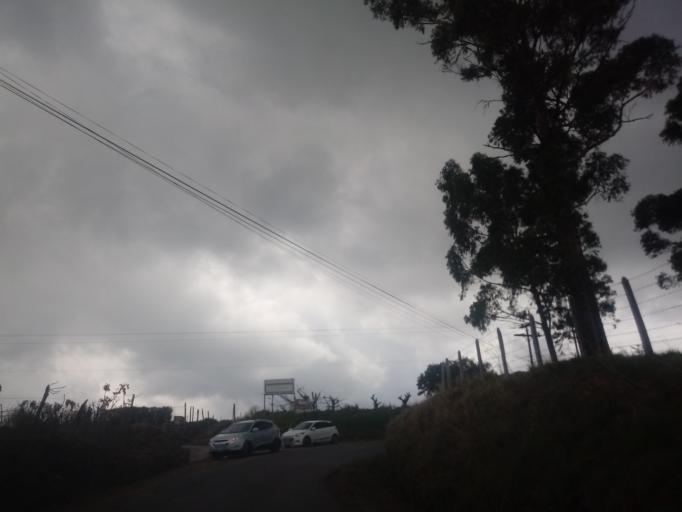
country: CR
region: Cartago
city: Cot
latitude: 9.9311
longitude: -83.8844
